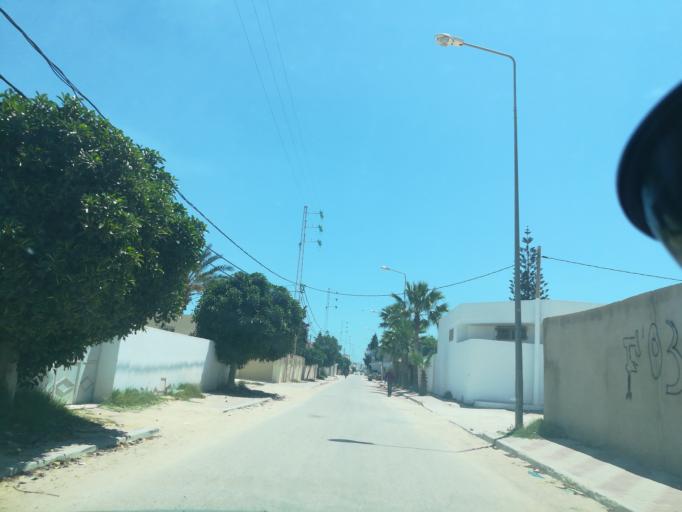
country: TN
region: Safaqis
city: Al Qarmadah
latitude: 34.8218
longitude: 10.7563
